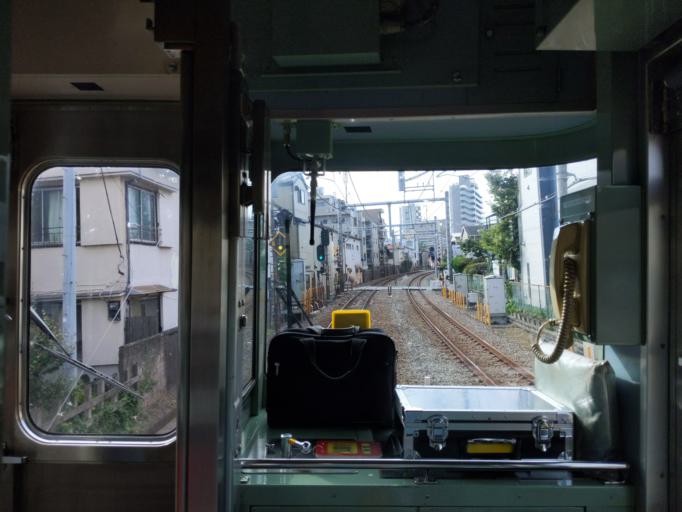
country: JP
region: Tokyo
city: Tokyo
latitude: 35.7284
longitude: 139.6867
